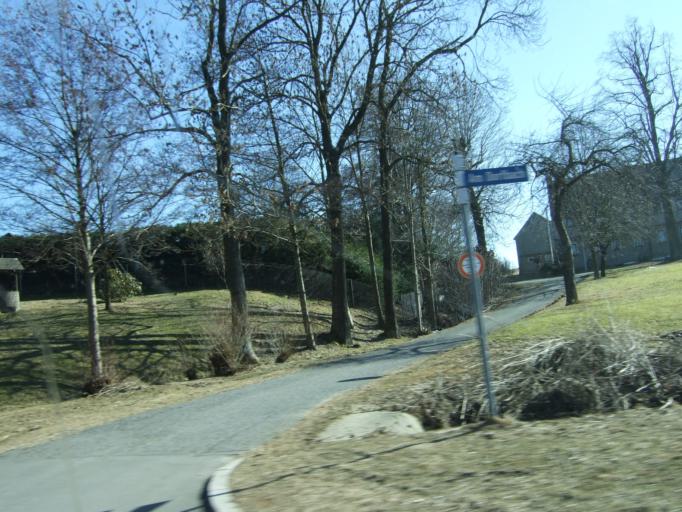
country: DE
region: Saxony
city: Oberschona
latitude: 50.8609
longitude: 13.2481
